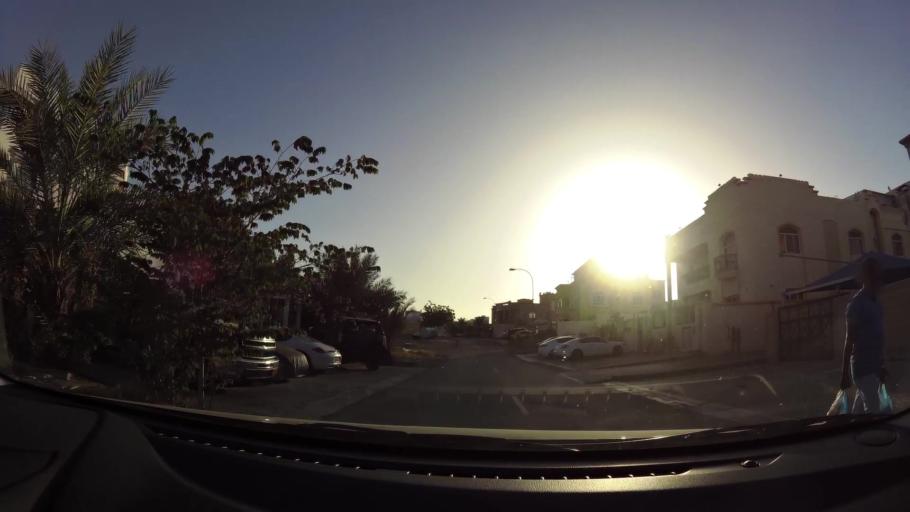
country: OM
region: Muhafazat Masqat
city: As Sib al Jadidah
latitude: 23.6083
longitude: 58.2291
